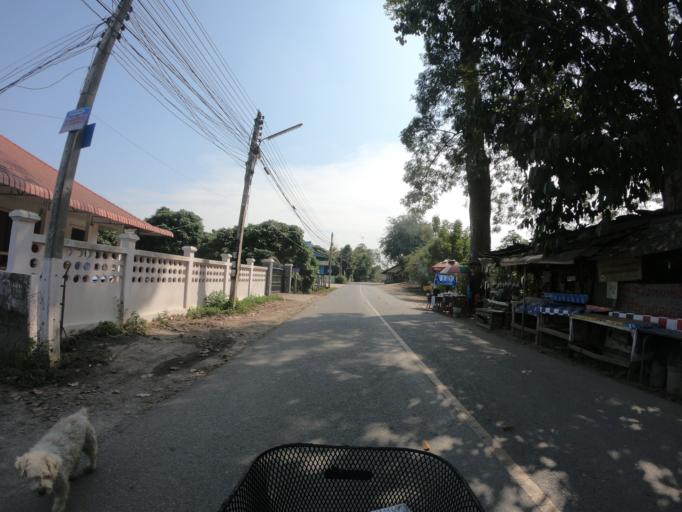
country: TH
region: Chiang Mai
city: Saraphi
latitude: 18.7058
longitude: 99.0513
